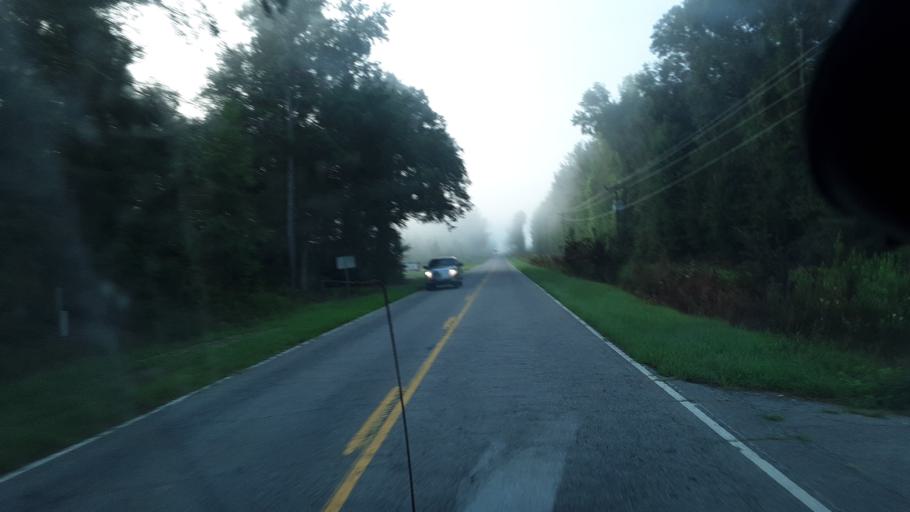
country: US
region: South Carolina
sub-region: Clarendon County
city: Manning
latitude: 33.7615
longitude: -80.0323
